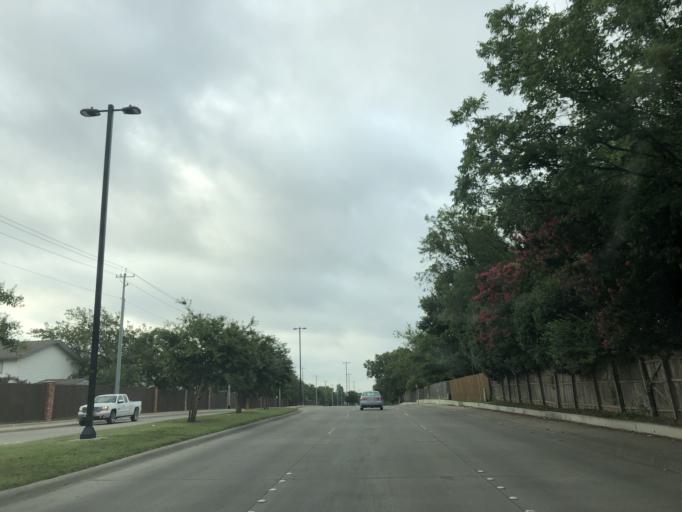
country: US
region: Texas
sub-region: Dallas County
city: Garland
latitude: 32.8599
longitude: -96.6410
